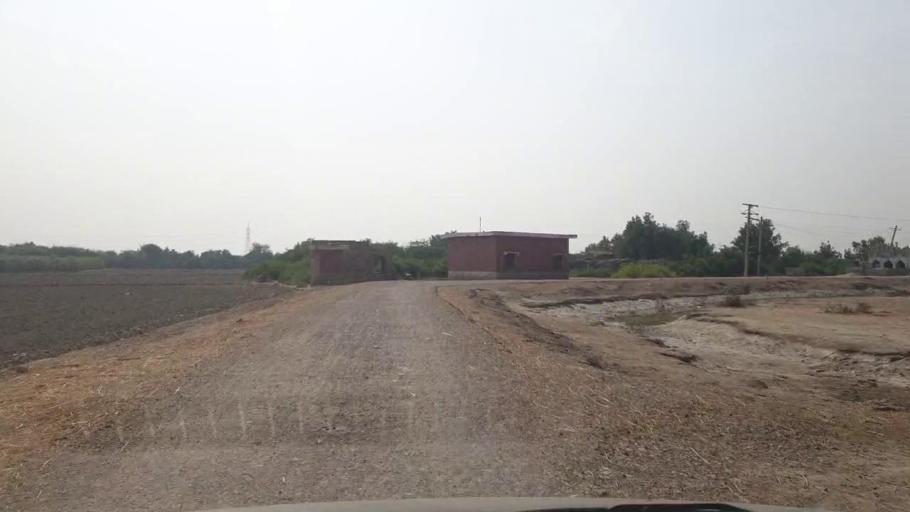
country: PK
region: Sindh
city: Tando Muhammad Khan
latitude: 25.1164
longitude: 68.3867
